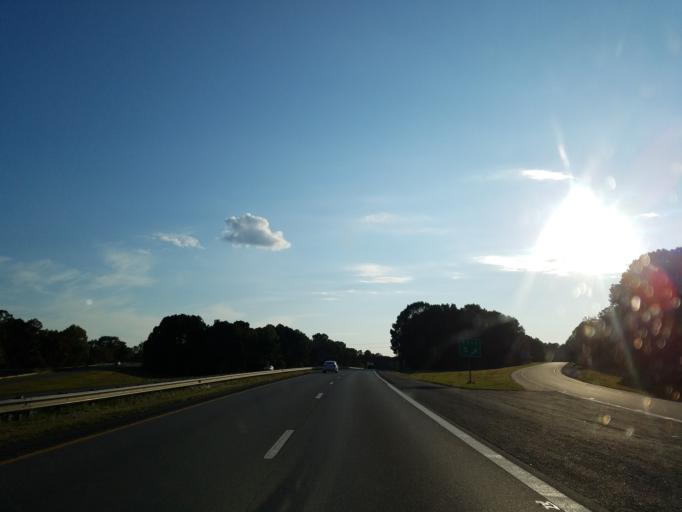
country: US
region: North Carolina
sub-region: Cleveland County
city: White Plains
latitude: 35.2011
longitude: -81.3668
